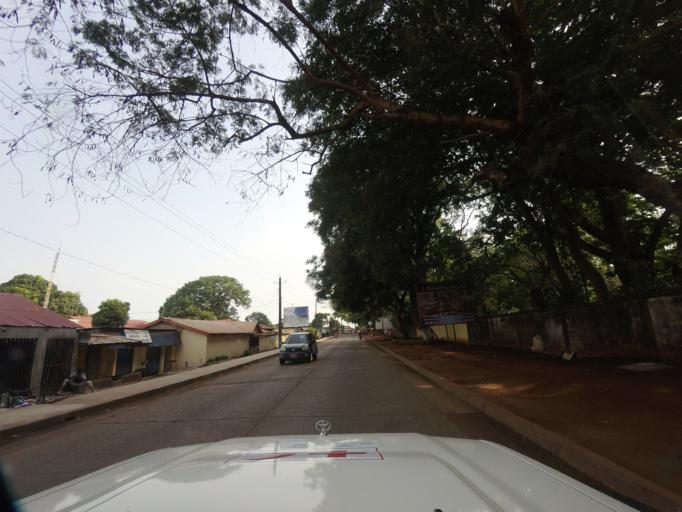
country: GN
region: Conakry
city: Camayenne
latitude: 9.5316
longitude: -13.6871
